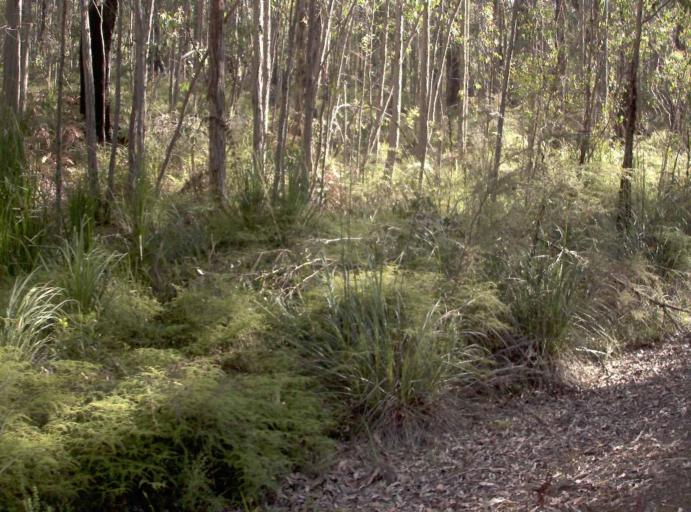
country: AU
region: Victoria
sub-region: East Gippsland
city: Lakes Entrance
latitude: -37.6228
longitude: 148.5091
